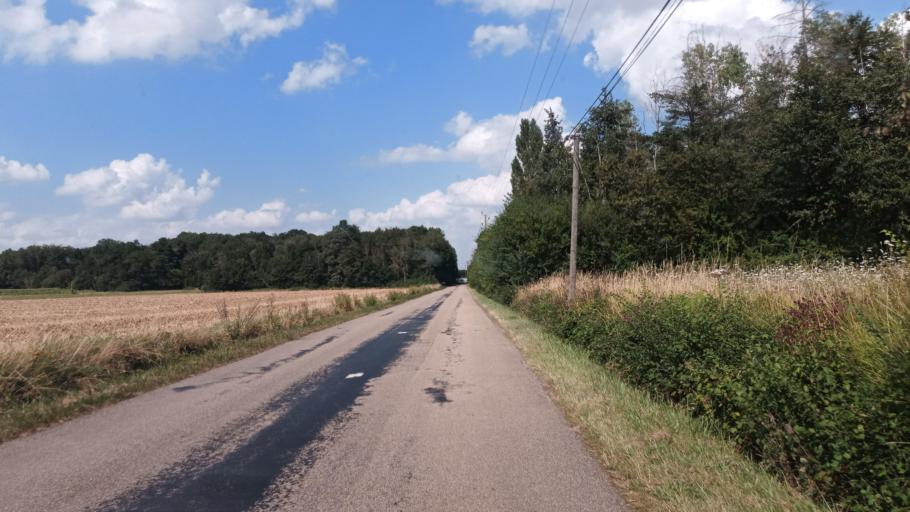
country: FR
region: Centre
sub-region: Departement du Loiret
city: Courtenay
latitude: 48.0049
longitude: 3.1509
